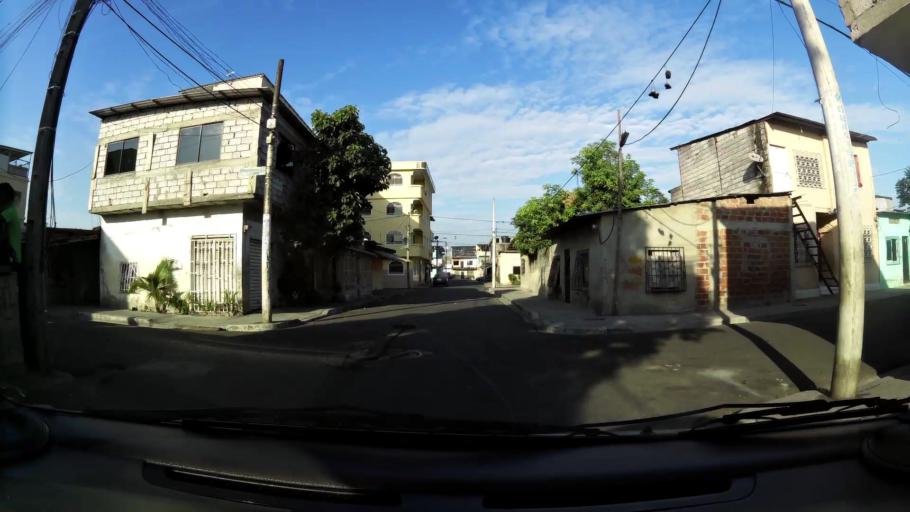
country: EC
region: Guayas
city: Guayaquil
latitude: -2.2282
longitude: -79.9113
